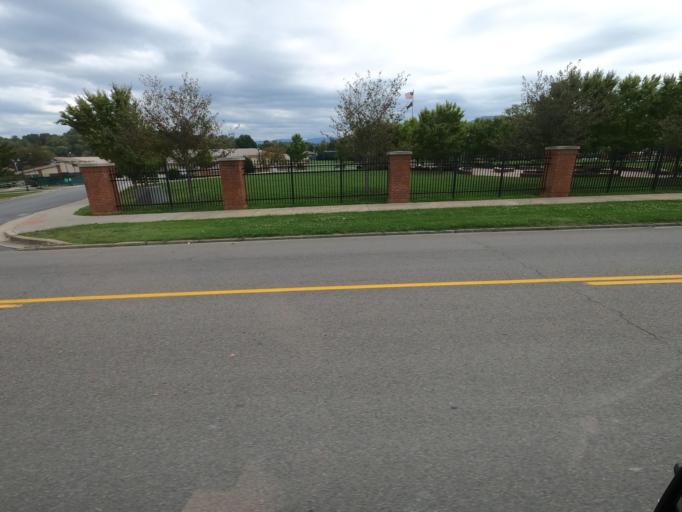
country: US
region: Tennessee
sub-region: Washington County
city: Johnson City
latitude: 36.3211
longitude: -82.3415
